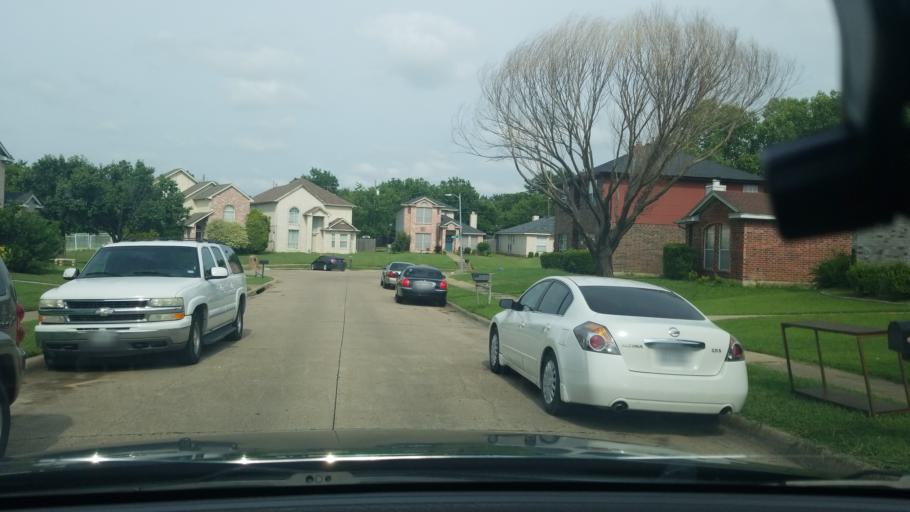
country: US
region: Texas
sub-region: Dallas County
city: Balch Springs
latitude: 32.7583
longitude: -96.6284
